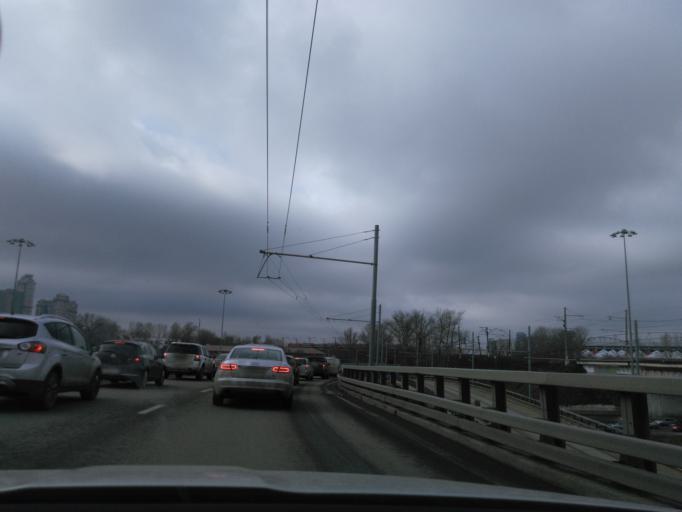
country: RU
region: Moscow
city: Pokrovskoye-Streshnevo
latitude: 55.8211
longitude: 37.4498
